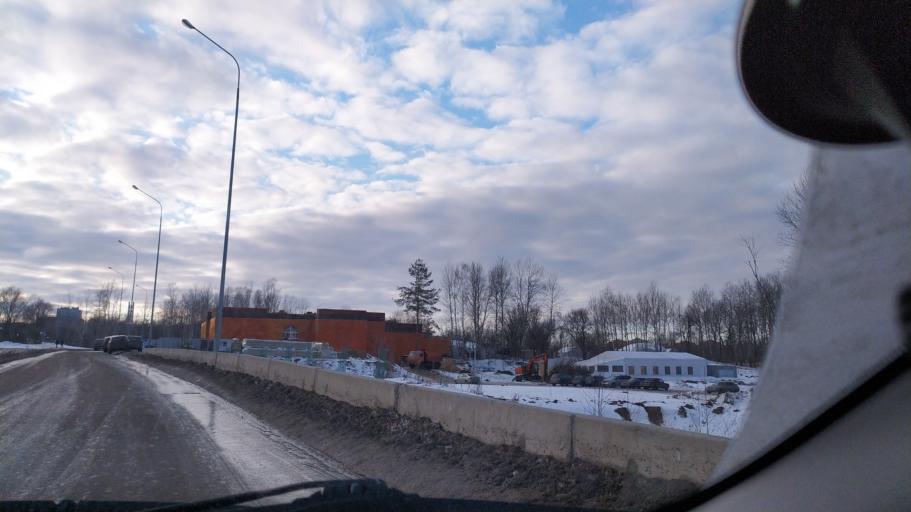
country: RU
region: Chuvashia
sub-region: Cheboksarskiy Rayon
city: Cheboksary
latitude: 56.1492
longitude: 47.2122
